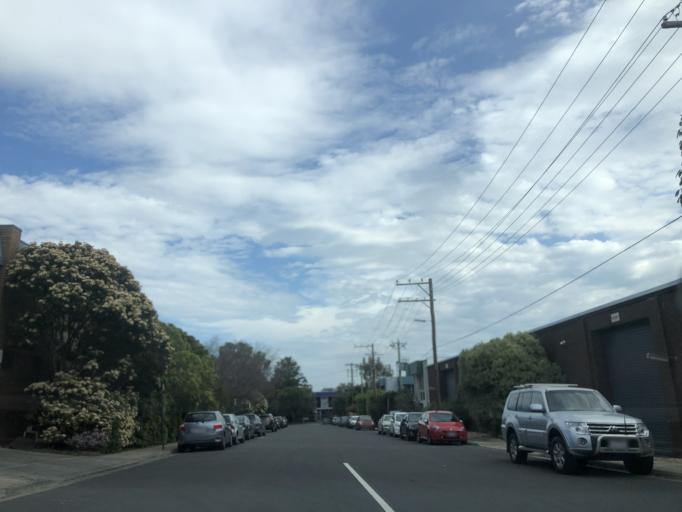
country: AU
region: Victoria
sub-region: Monash
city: Notting Hill
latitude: -37.9106
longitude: 145.1467
